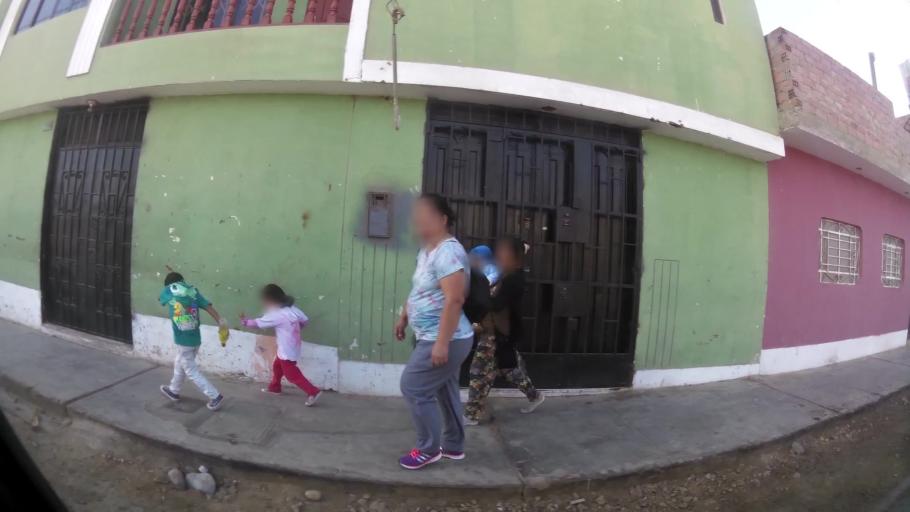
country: PE
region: Lima
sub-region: Huaura
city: Huacho
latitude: -11.1115
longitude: -77.6031
